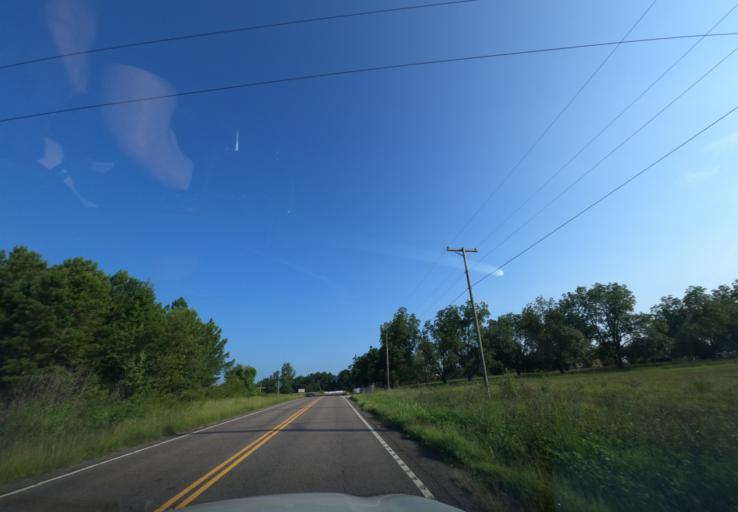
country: US
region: South Carolina
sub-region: Edgefield County
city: Murphys Estates
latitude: 33.6152
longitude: -81.9665
